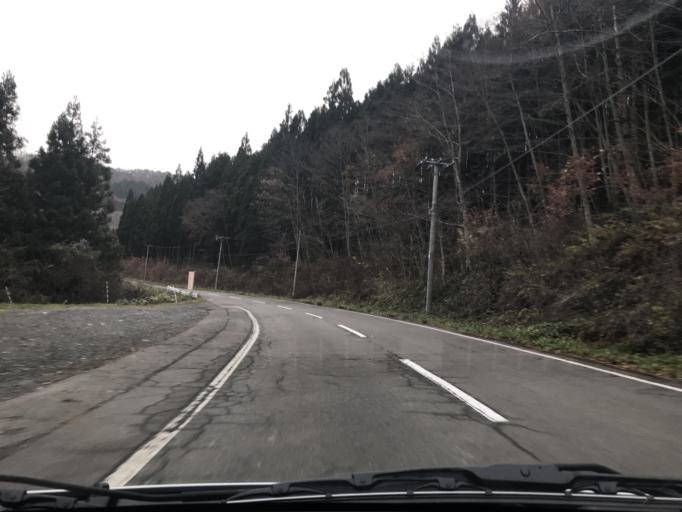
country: JP
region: Iwate
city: Tono
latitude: 39.1786
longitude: 141.3625
